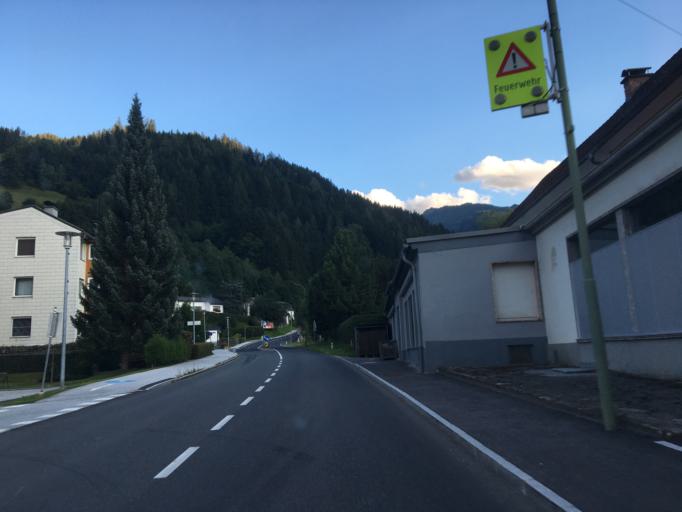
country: AT
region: Styria
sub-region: Politischer Bezirk Liezen
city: Trieben
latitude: 47.4844
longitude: 14.4867
